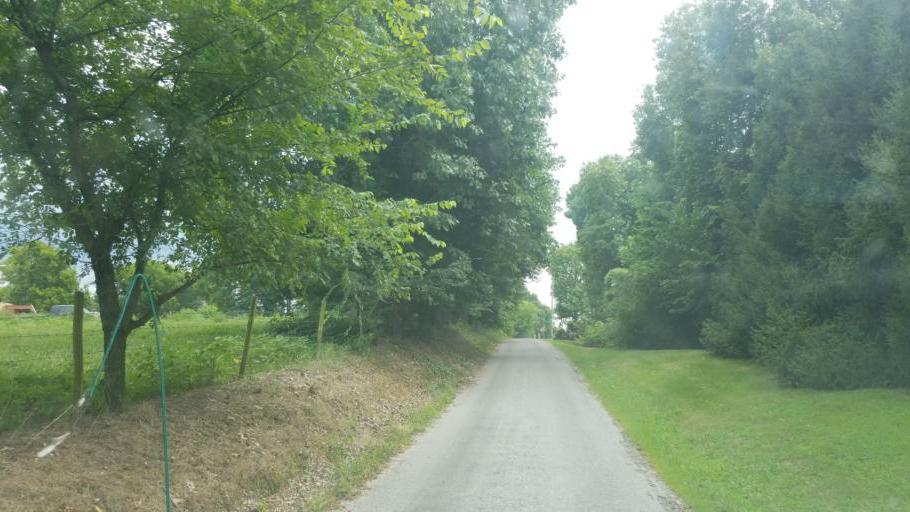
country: US
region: Illinois
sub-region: Jackson County
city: Murphysboro
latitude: 37.7045
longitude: -89.3478
